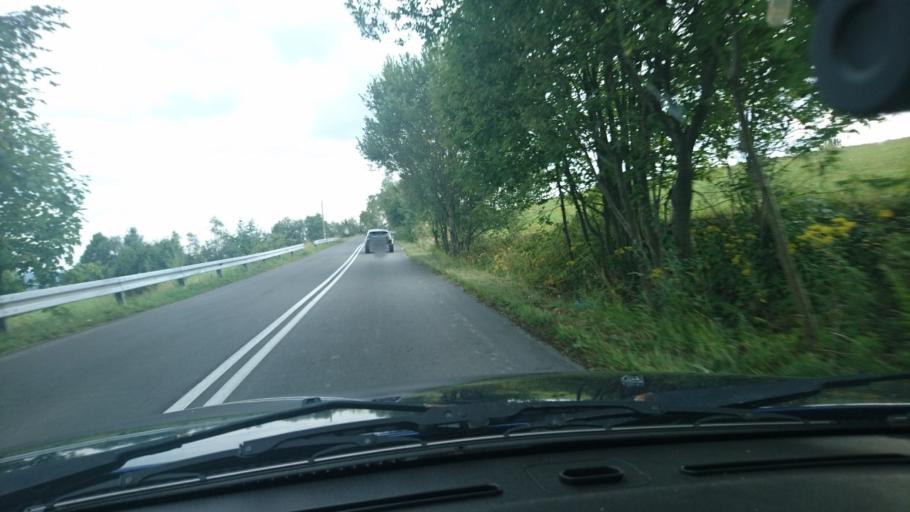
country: PL
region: Silesian Voivodeship
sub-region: Powiat zywiecki
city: Laliki
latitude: 49.5479
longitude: 18.9933
